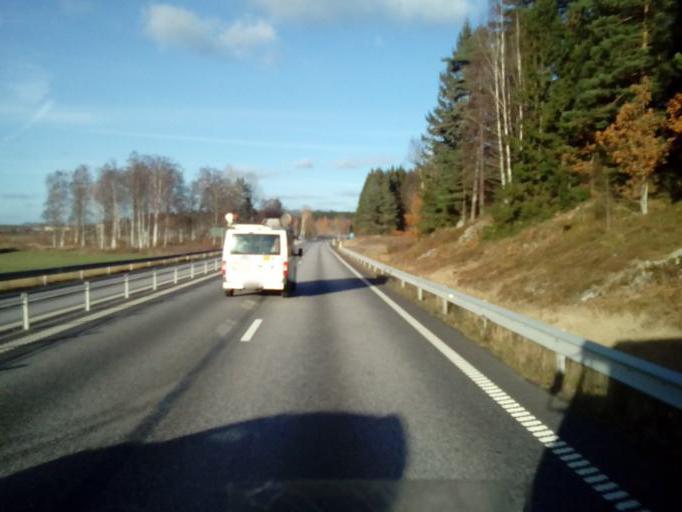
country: SE
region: Kalmar
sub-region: Vimmerby Kommun
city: Vimmerby
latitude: 57.6983
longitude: 16.0158
